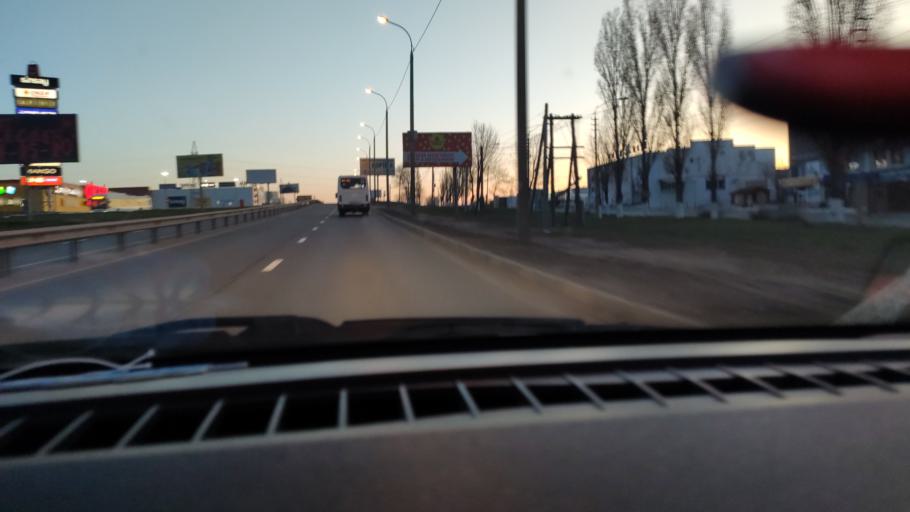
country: RU
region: Saratov
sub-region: Saratovskiy Rayon
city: Saratov
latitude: 51.6197
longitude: 45.9744
